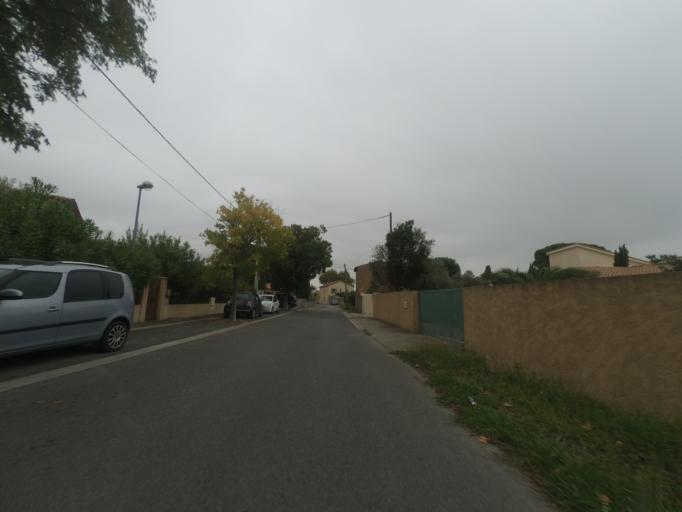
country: FR
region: Languedoc-Roussillon
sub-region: Departement des Pyrenees-Orientales
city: Saint-Esteve
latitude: 42.7050
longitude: 2.8455
